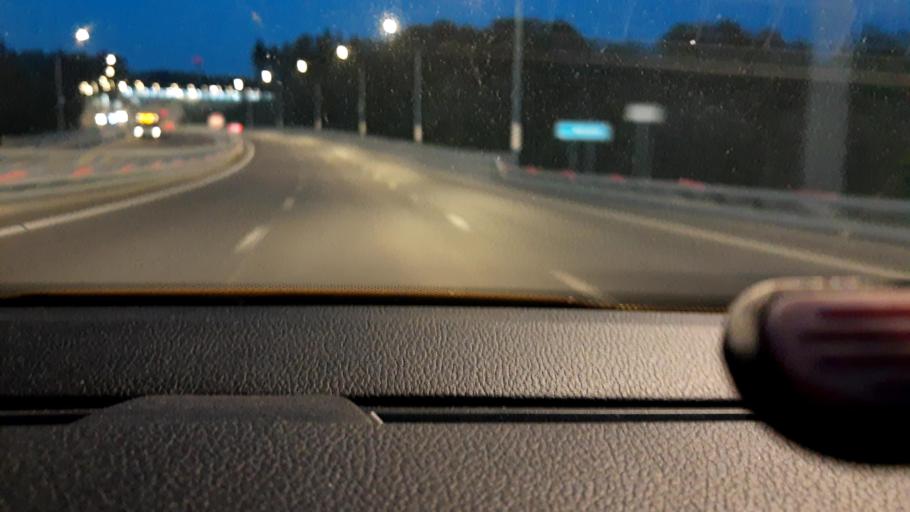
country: RU
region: Moskovskaya
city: Filimonki
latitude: 55.5654
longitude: 37.3479
